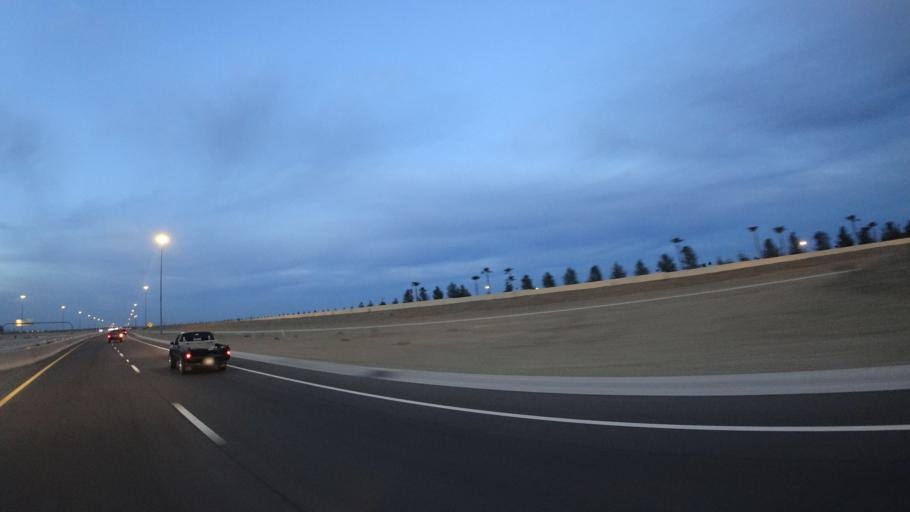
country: US
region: Arizona
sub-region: Maricopa County
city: Litchfield Park
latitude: 33.4686
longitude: -112.4261
